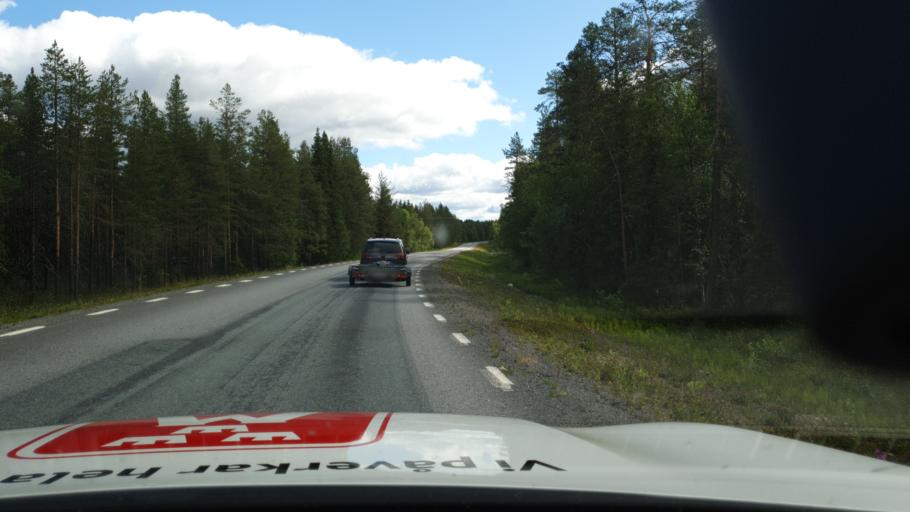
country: SE
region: Vaesterbotten
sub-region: Mala Kommun
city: Mala
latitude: 65.1476
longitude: 18.5746
